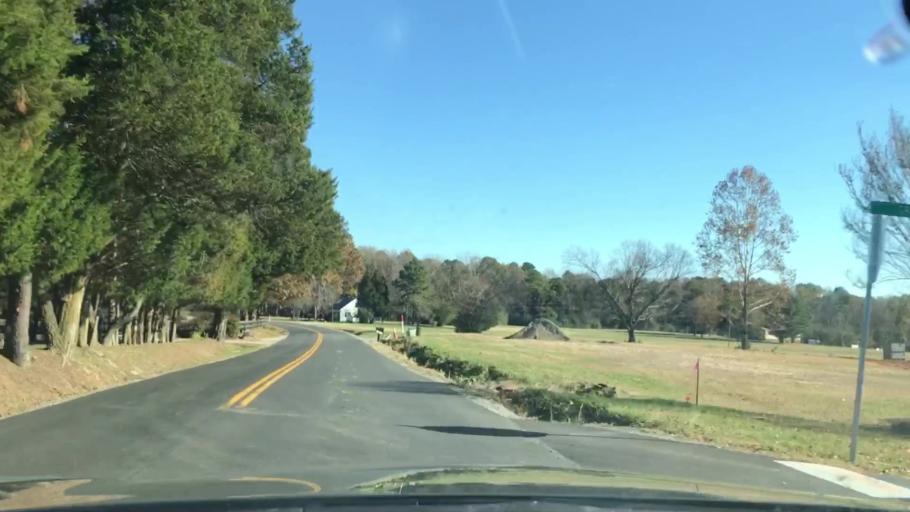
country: US
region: Virginia
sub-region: Henrico County
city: Short Pump
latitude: 37.6669
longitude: -77.7019
